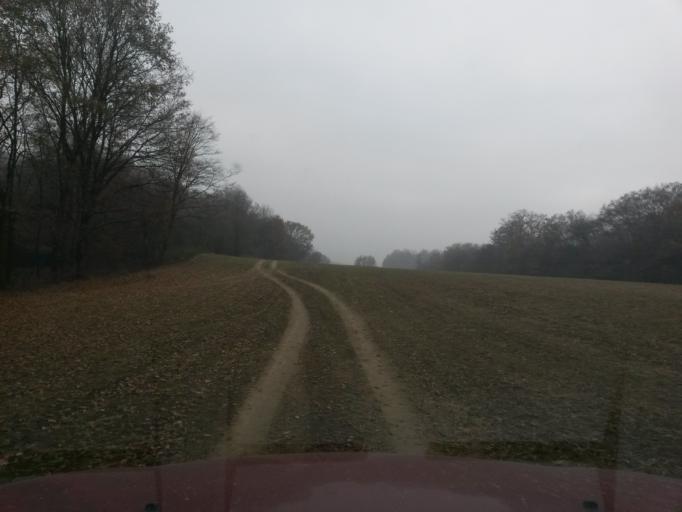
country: SK
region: Presovsky
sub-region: Okres Presov
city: Presov
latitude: 48.8934
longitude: 21.2996
